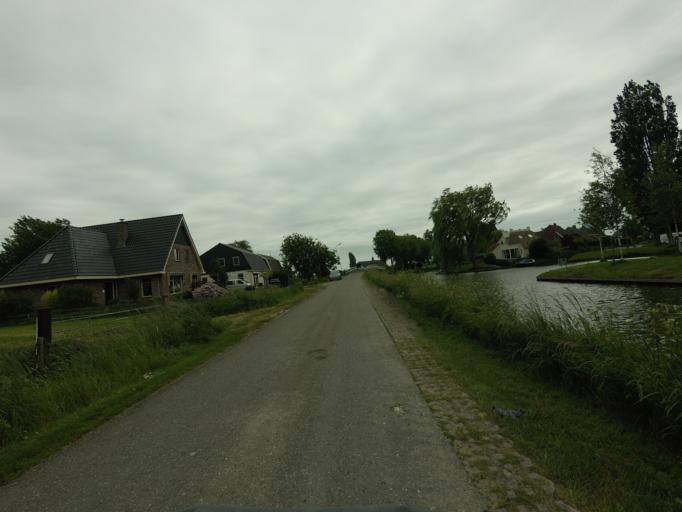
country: NL
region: North Holland
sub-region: Gemeente Medemblik
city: Medemblik
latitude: 52.7612
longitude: 5.1098
